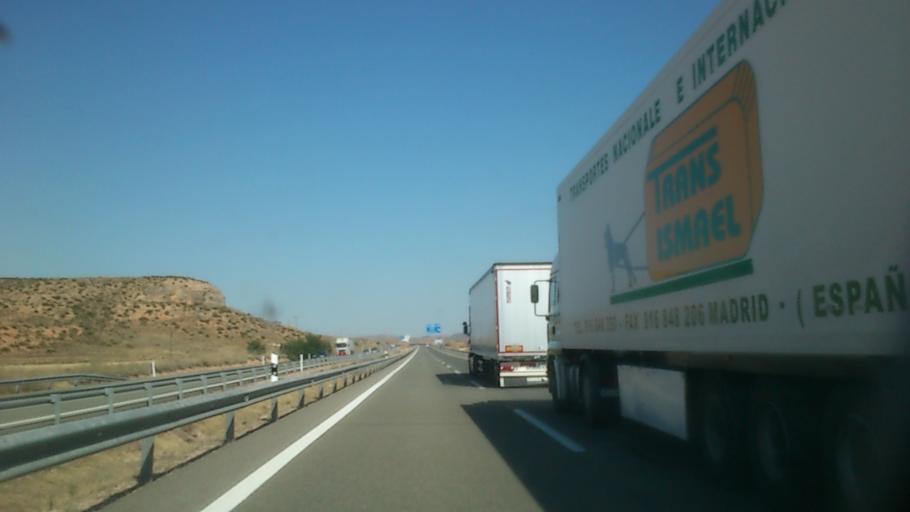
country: ES
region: Aragon
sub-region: Provincia de Zaragoza
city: Cetina
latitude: 41.3063
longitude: -1.9834
